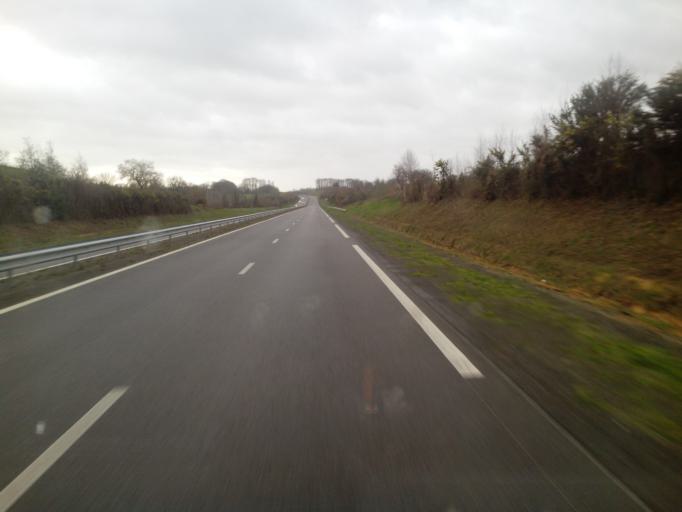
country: FR
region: Brittany
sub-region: Departement d'Ille-et-Vilaine
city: Betton
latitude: 48.1908
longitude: -1.6231
